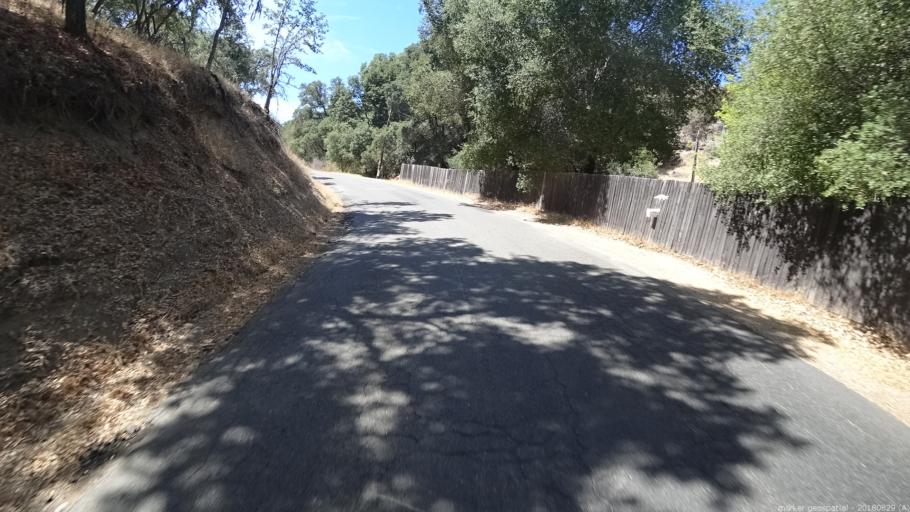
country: US
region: California
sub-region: San Luis Obispo County
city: Lake Nacimiento
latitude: 35.8239
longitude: -121.0517
